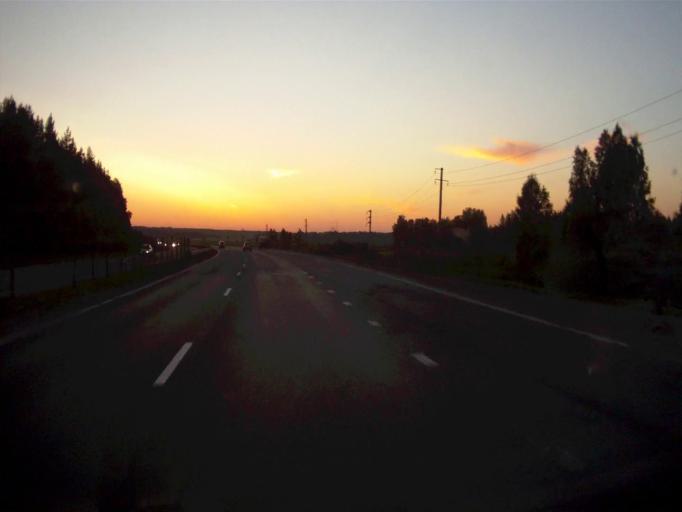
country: RU
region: Chelyabinsk
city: Roshchino
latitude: 55.1938
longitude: 61.2160
